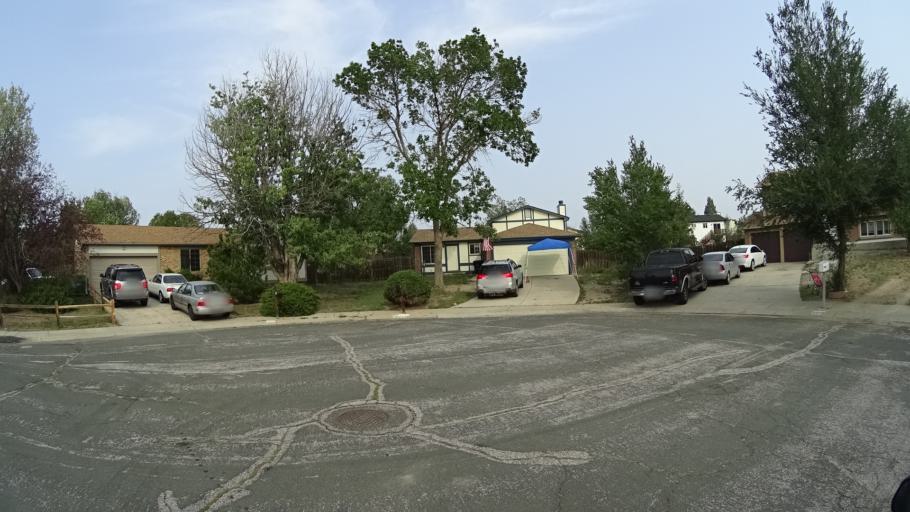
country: US
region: Colorado
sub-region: El Paso County
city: Cimarron Hills
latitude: 38.8147
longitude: -104.7350
